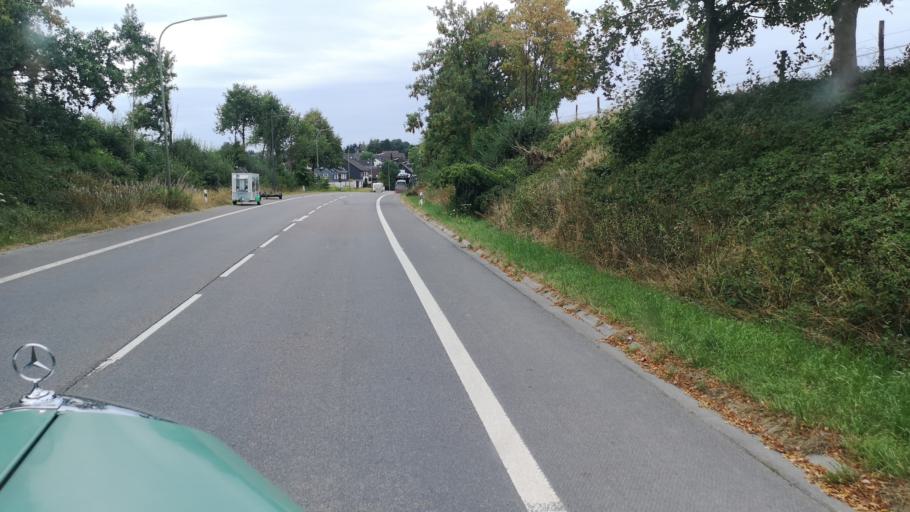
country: DE
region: North Rhine-Westphalia
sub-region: Regierungsbezirk Koln
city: Kurten
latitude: 51.0665
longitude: 7.2426
